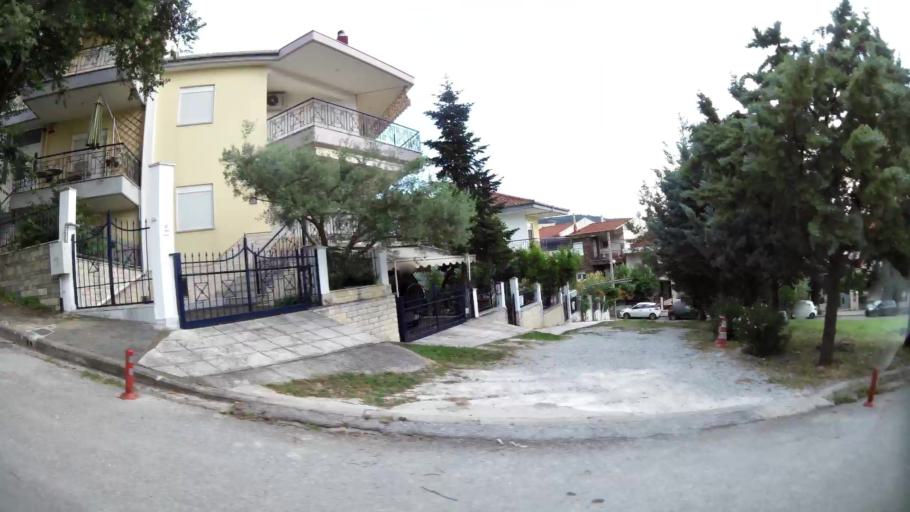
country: GR
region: Central Macedonia
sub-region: Nomos Thessalonikis
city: Pefka
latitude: 40.6630
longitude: 22.9852
